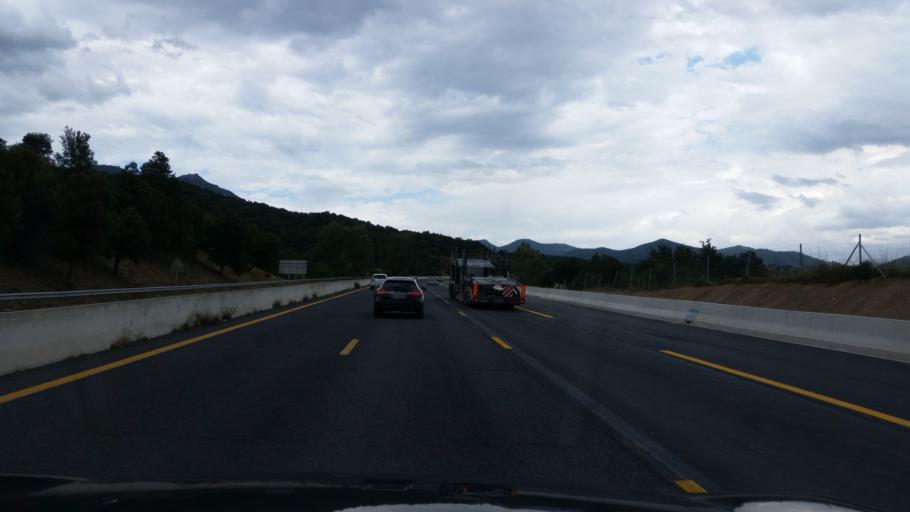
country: FR
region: Languedoc-Roussillon
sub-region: Departement des Pyrenees-Orientales
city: Maureillas-las-Illas
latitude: 42.4965
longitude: 2.8255
